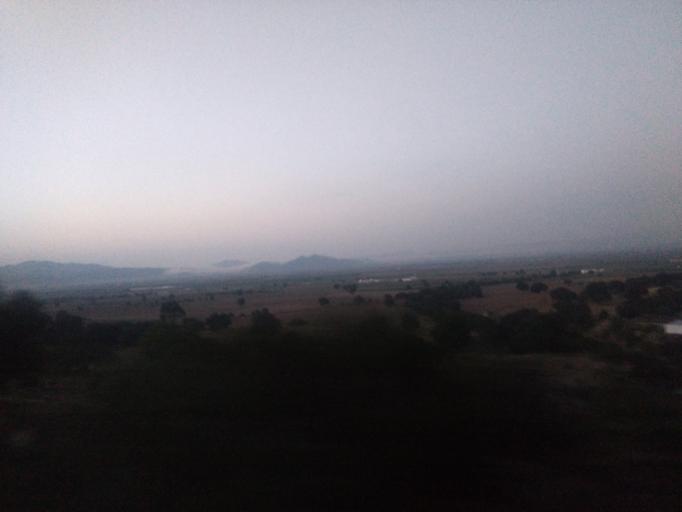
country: MX
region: Puebla
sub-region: Oriental
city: San Antonio Virreyes
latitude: 19.4109
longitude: -97.6565
